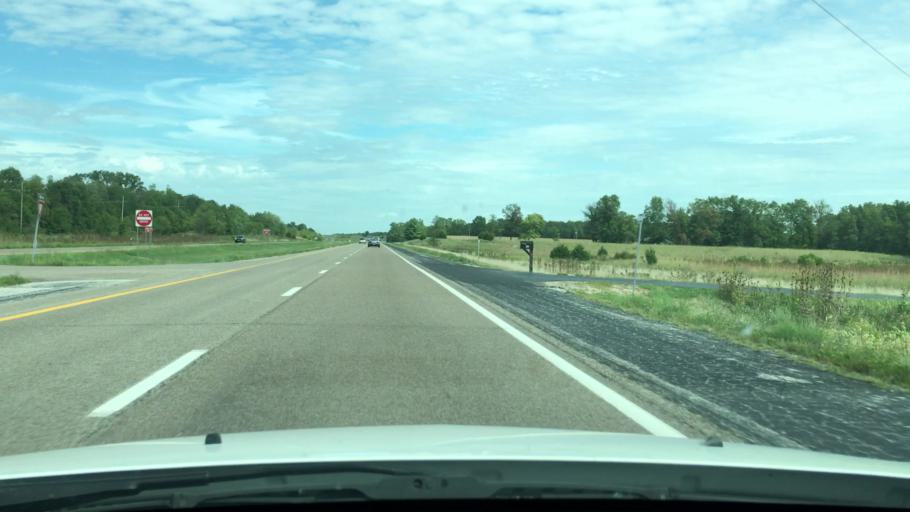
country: US
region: Missouri
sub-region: Audrain County
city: Mexico
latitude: 39.0513
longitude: -91.8940
